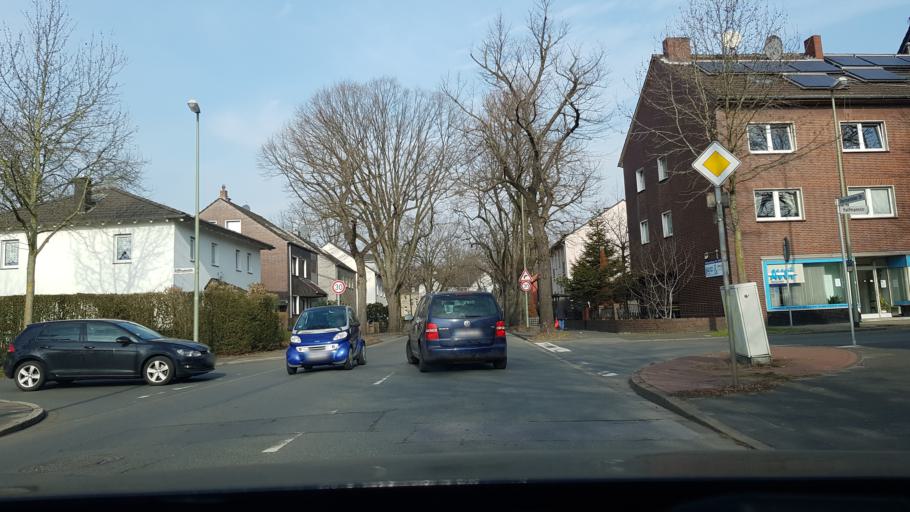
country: DE
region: North Rhine-Westphalia
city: Meiderich
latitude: 51.5029
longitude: 6.7959
